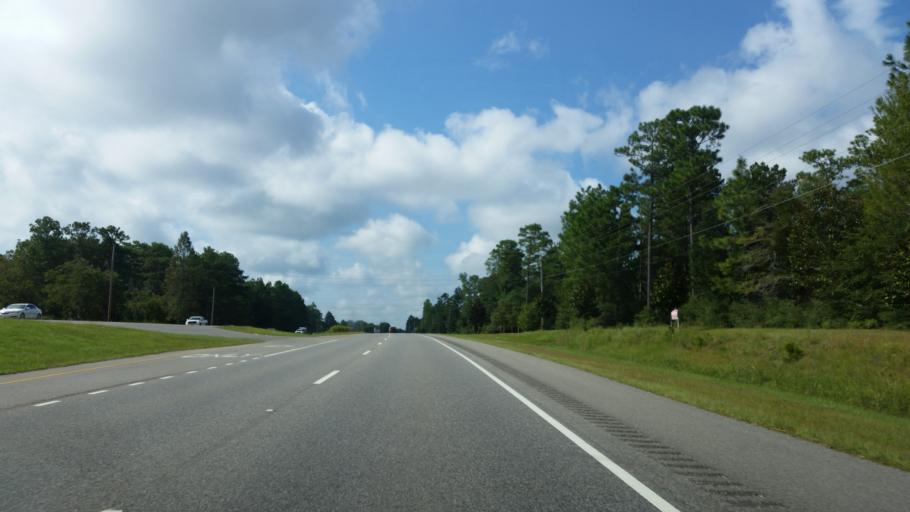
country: US
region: Alabama
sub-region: Baldwin County
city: Bay Minette
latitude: 30.9226
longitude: -87.7734
